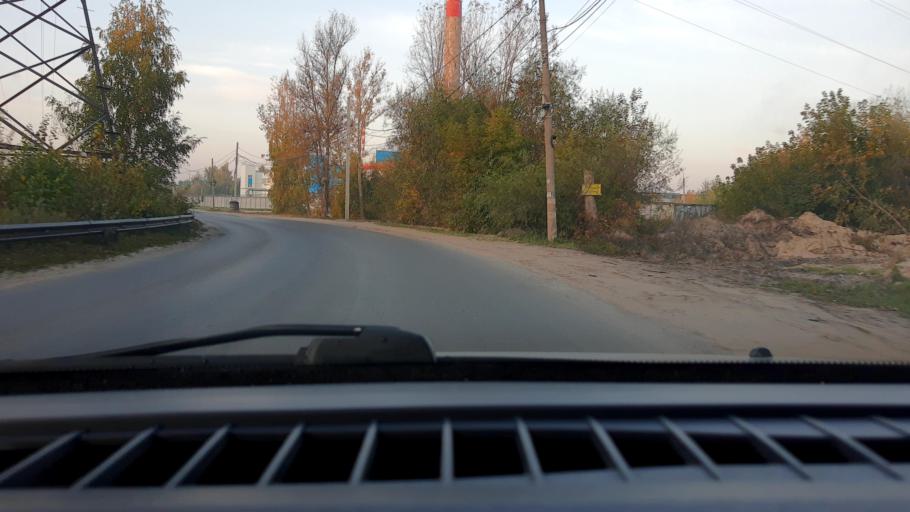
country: RU
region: Nizjnij Novgorod
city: Gorbatovka
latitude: 56.3731
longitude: 43.8003
